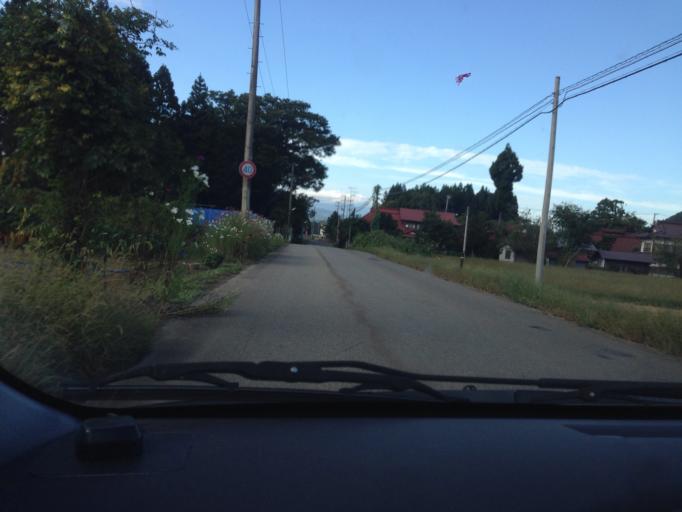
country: JP
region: Fukushima
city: Kitakata
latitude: 37.5805
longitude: 139.7710
